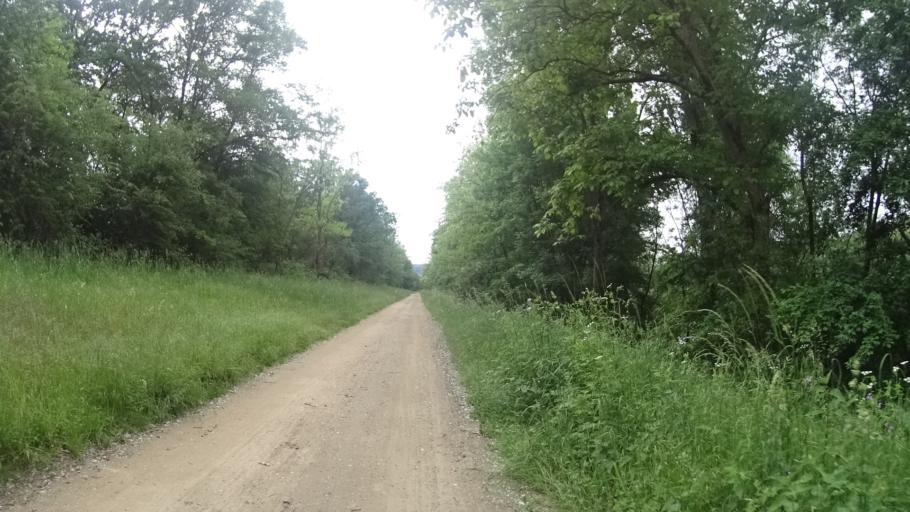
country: FR
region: Alsace
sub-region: Departement du Haut-Rhin
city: Kembs
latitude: 47.6930
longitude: 7.5154
